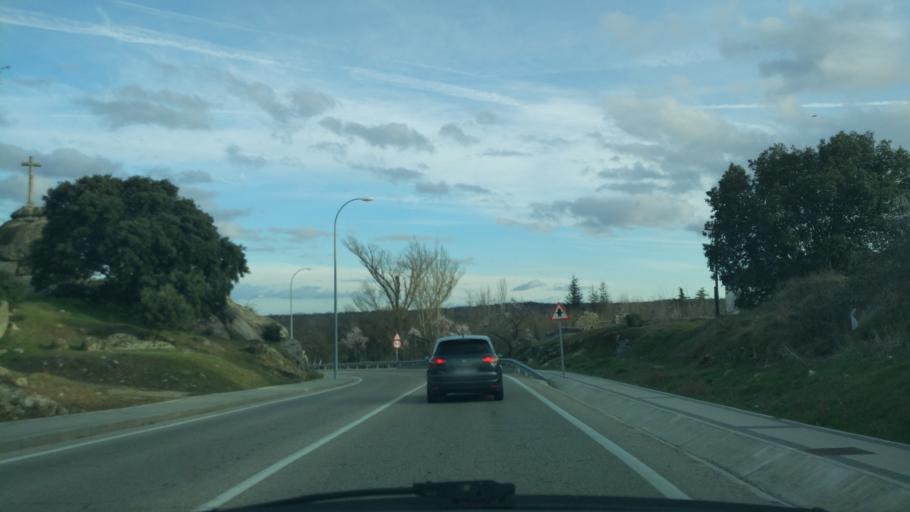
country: ES
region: Madrid
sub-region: Provincia de Madrid
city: El Escorial
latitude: 40.5836
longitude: -4.1226
